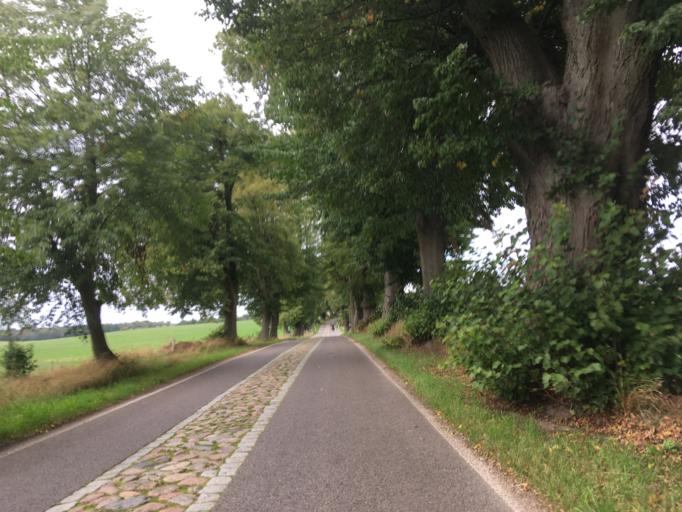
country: DE
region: Brandenburg
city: Joachimsthal
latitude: 53.0173
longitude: 13.7597
